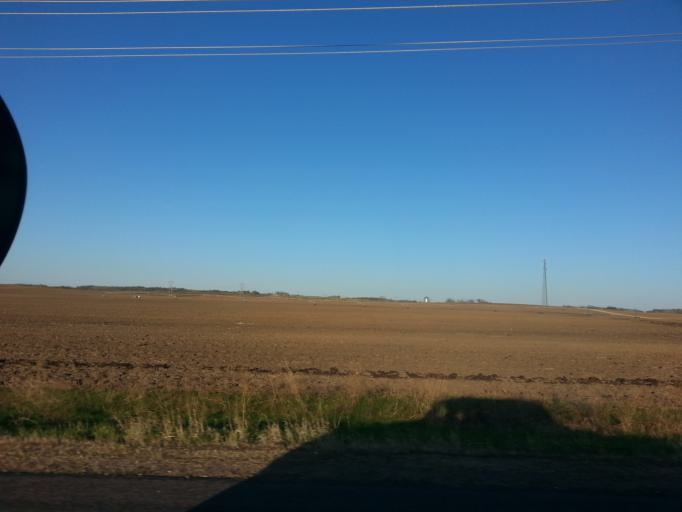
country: US
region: Wisconsin
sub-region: Pierce County
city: Prescott
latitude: 44.6172
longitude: -92.7724
